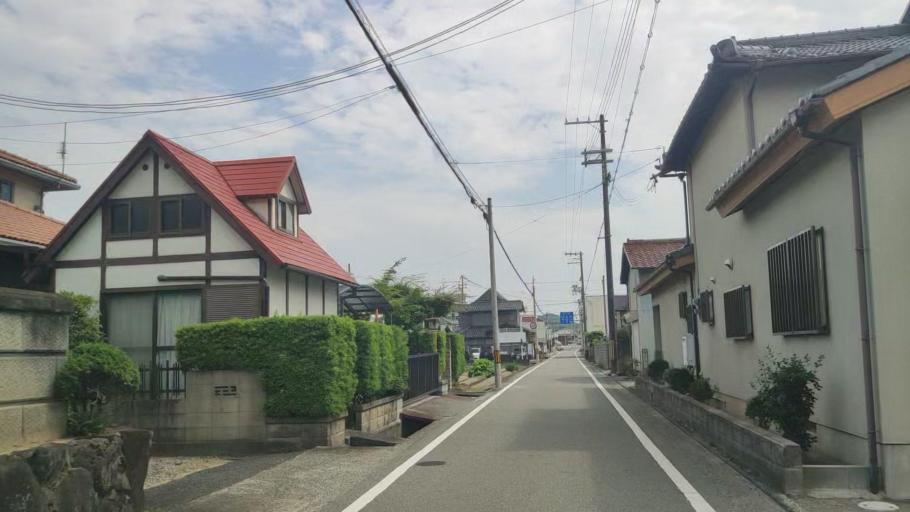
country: JP
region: Hyogo
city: Tatsunocho-tominaga
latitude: 34.8323
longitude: 134.6024
